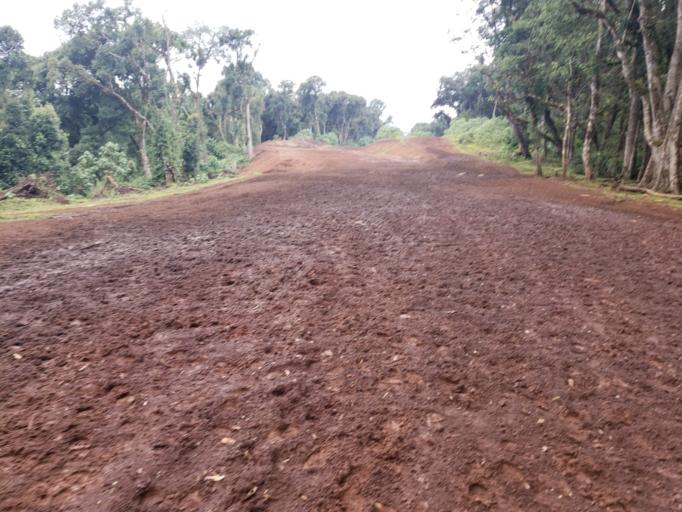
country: ET
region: Oromiya
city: Dodola
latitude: 6.6121
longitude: 39.4180
